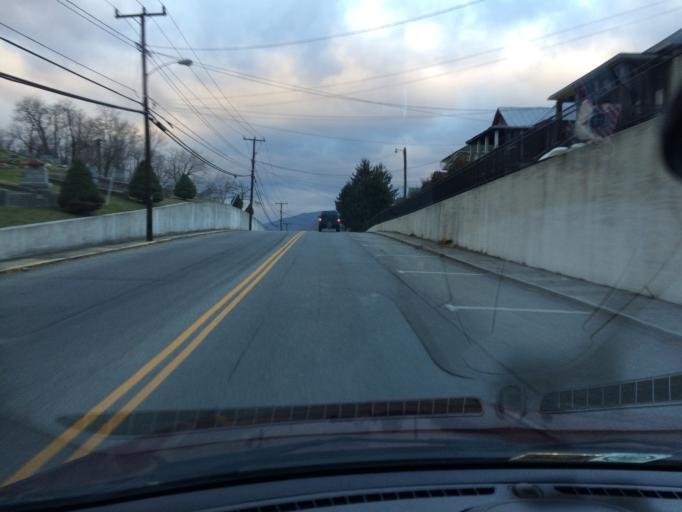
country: US
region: Virginia
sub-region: Alleghany County
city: Clifton Forge
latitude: 37.8156
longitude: -79.8167
